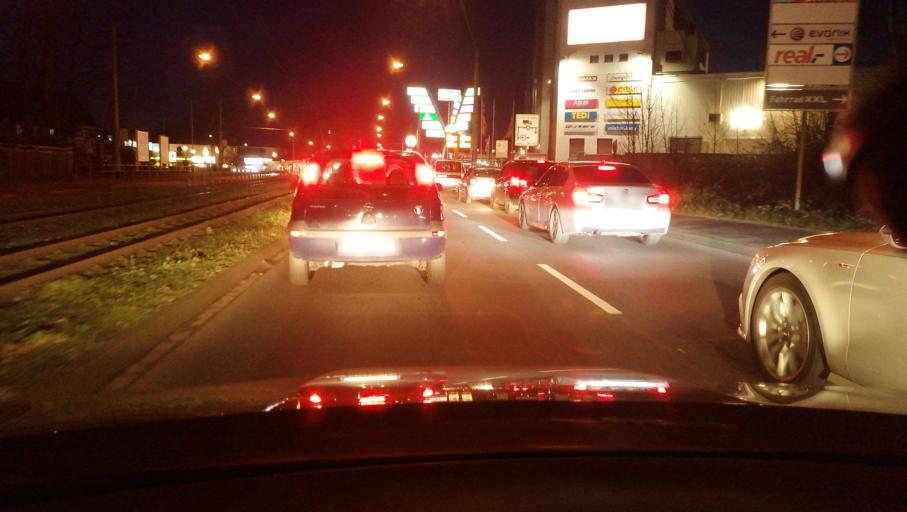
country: DE
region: North Rhine-Westphalia
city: Bochum-Hordel
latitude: 51.5061
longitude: 7.1901
